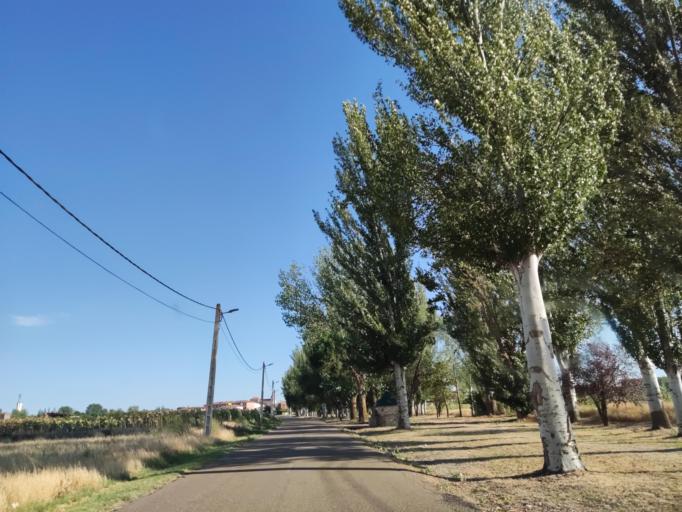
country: ES
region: Castille and Leon
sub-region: Provincia de Zamora
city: Villaralbo
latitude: 41.4982
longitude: -5.6856
